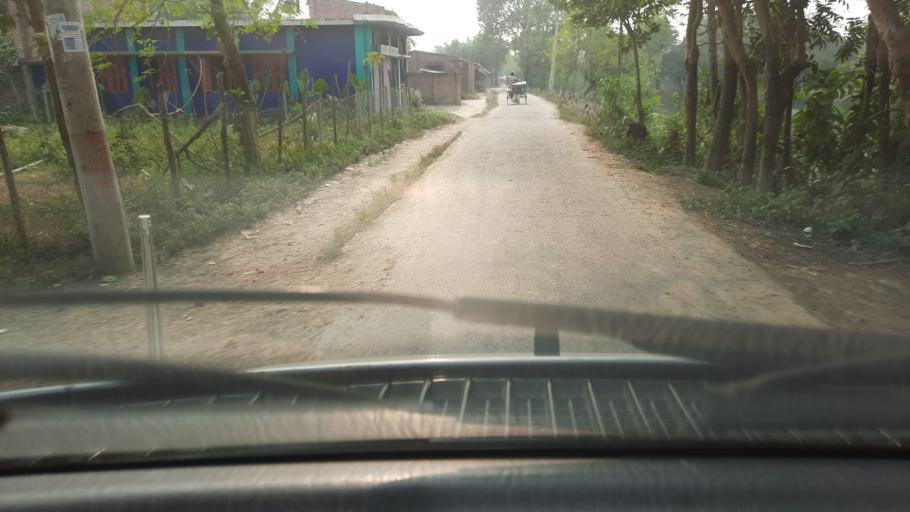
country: BD
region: Khulna
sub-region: Chuadanga
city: Nowlamary
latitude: 23.6044
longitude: 88.8585
